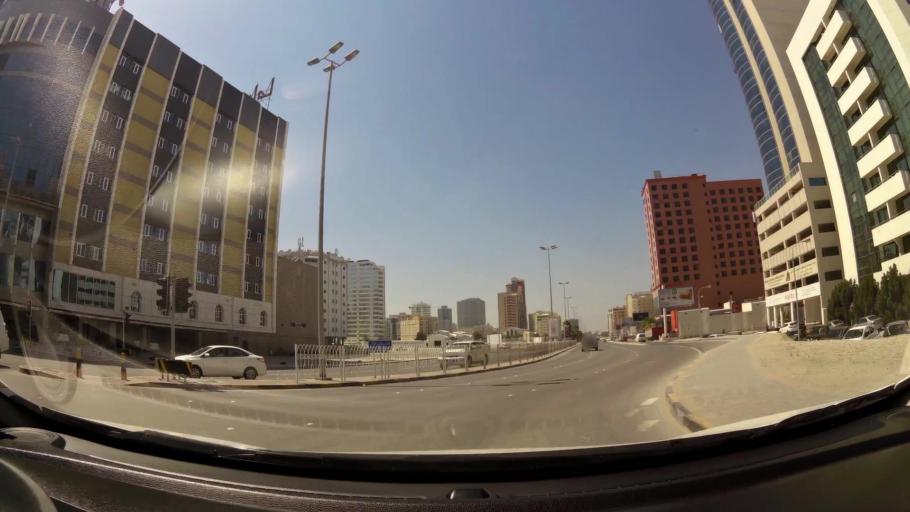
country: BH
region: Manama
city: Manama
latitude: 26.2167
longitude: 50.6096
